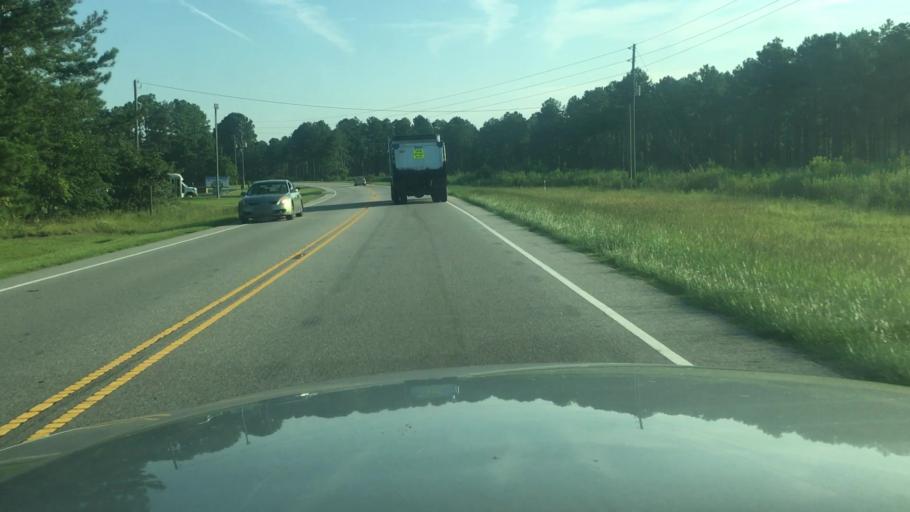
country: US
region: North Carolina
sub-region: Harnett County
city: Walkertown
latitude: 35.1931
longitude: -78.8499
